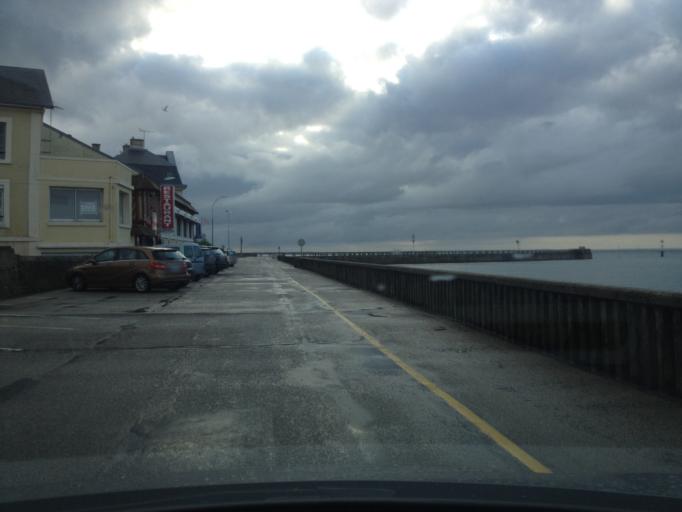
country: FR
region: Lower Normandy
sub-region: Departement du Calvados
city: Grandcamp-Maisy
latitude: 49.3893
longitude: -1.0453
